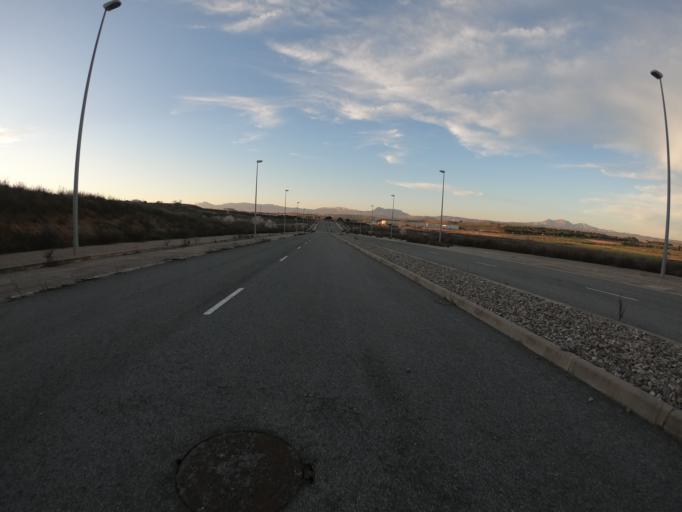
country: ES
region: Basque Country
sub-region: Provincia de Alava
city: Oyon
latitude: 42.4830
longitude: -2.4141
